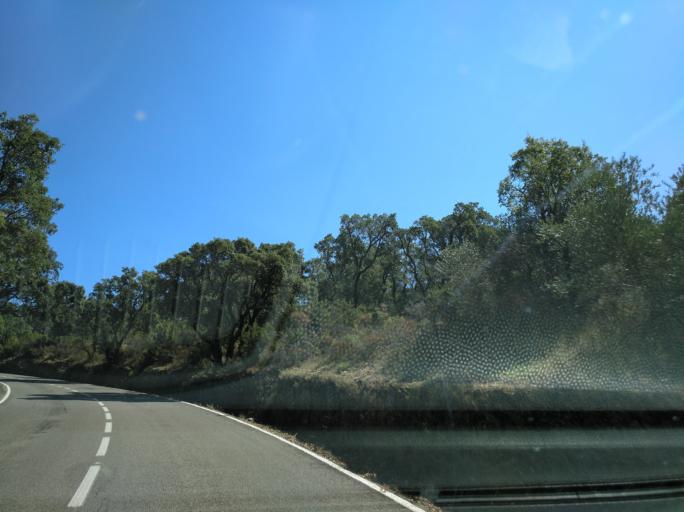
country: ES
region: Catalonia
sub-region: Provincia de Girona
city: Pau
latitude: 42.3332
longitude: 3.1168
